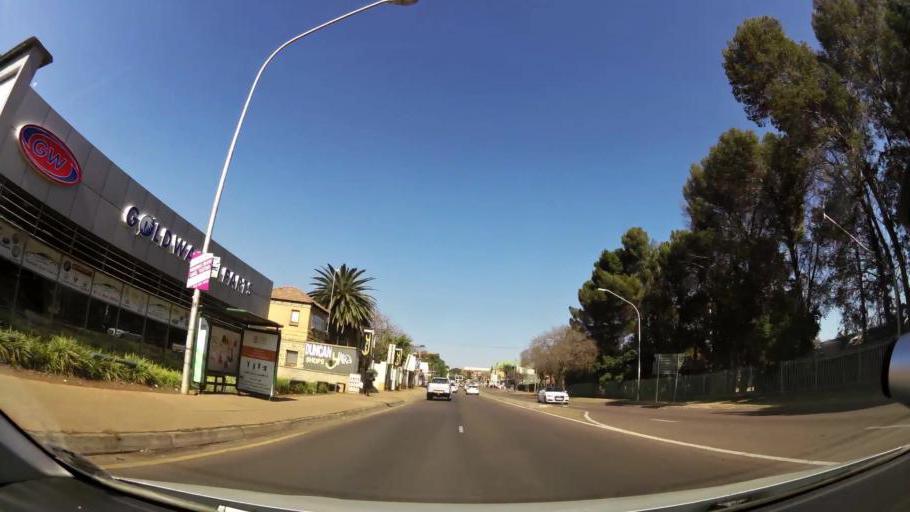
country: ZA
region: Gauteng
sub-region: City of Tshwane Metropolitan Municipality
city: Pretoria
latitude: -25.7510
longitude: 28.2402
